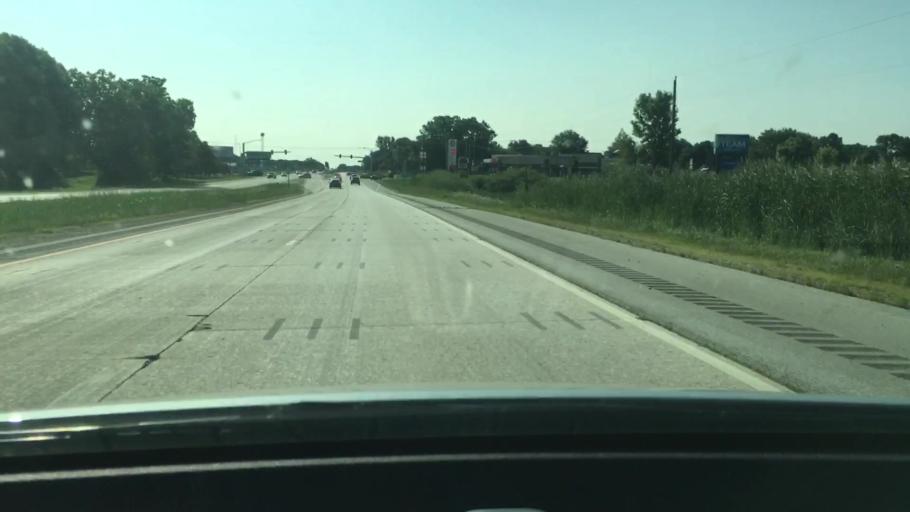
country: US
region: Wisconsin
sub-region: Brown County
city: Ashwaubenon
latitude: 44.4933
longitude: -88.1010
